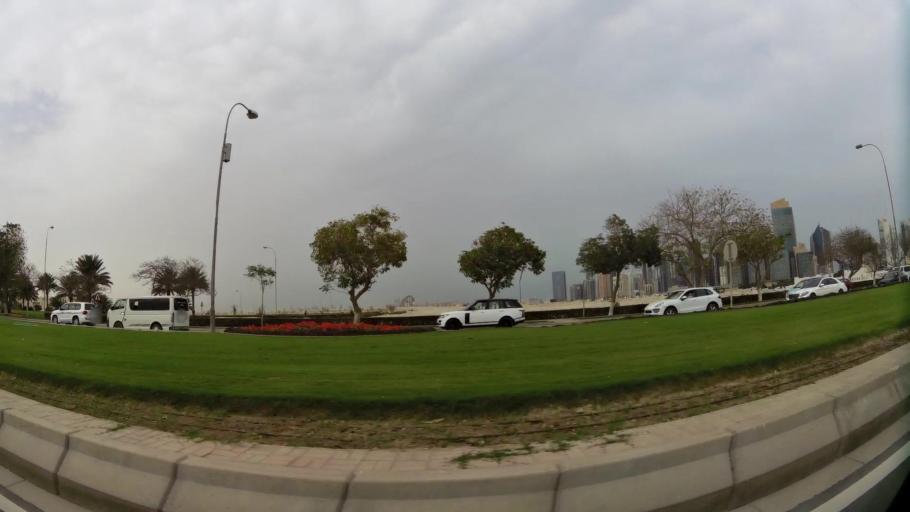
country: QA
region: Baladiyat ad Dawhah
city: Doha
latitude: 25.3127
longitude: 51.5078
